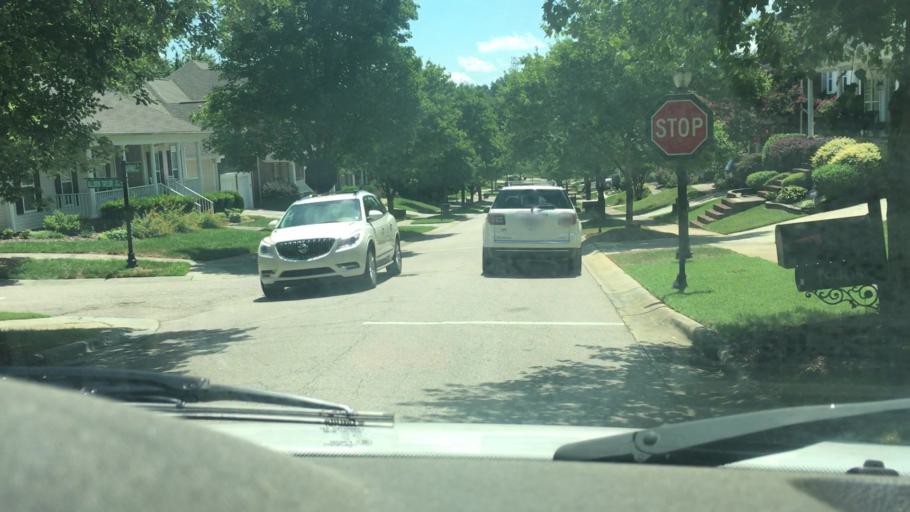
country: US
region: North Carolina
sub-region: Mecklenburg County
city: Cornelius
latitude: 35.4664
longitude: -80.8631
